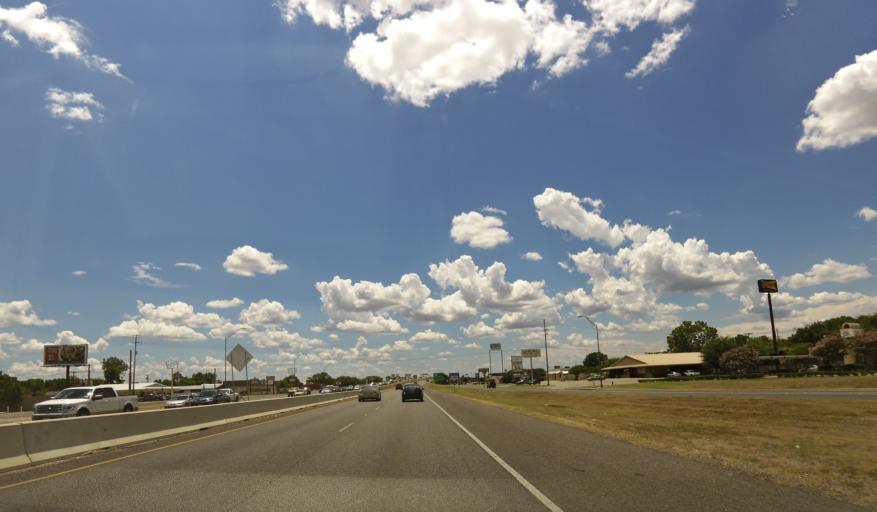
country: US
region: Texas
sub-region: Bastrop County
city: Bastrop
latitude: 30.1049
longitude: -97.3238
